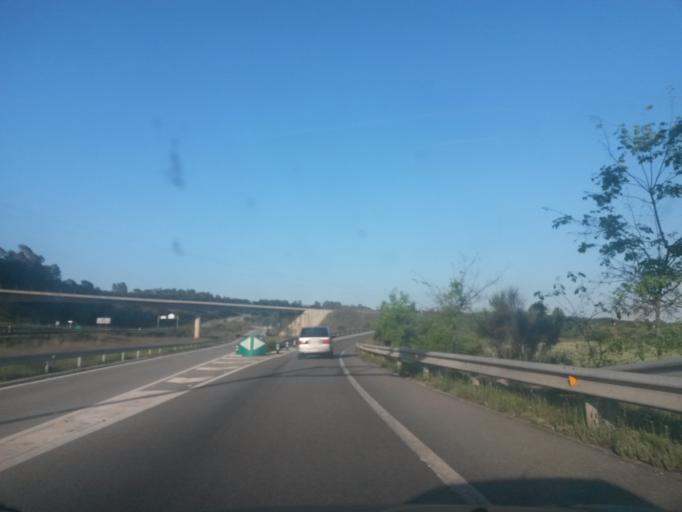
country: ES
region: Catalonia
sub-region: Provincia de Girona
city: Besalu
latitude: 42.2034
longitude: 2.7140
